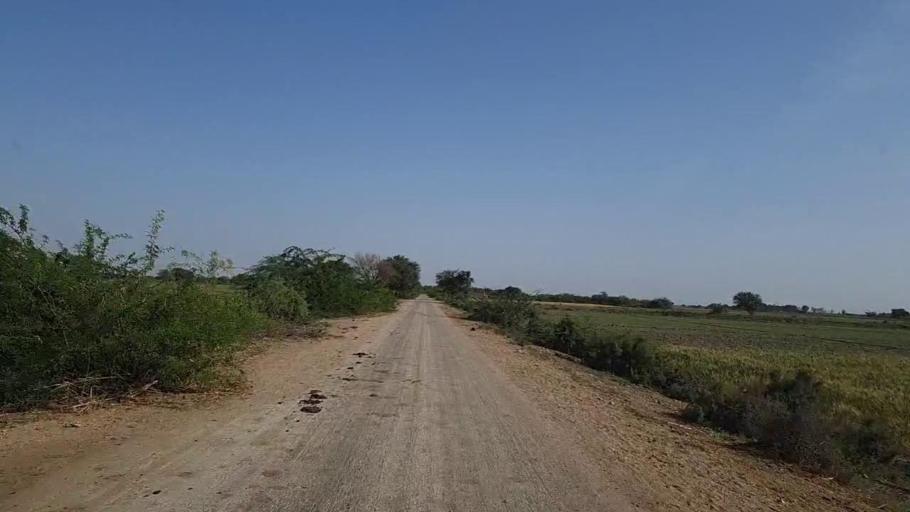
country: PK
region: Sindh
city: Kotri
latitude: 25.1492
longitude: 68.2939
